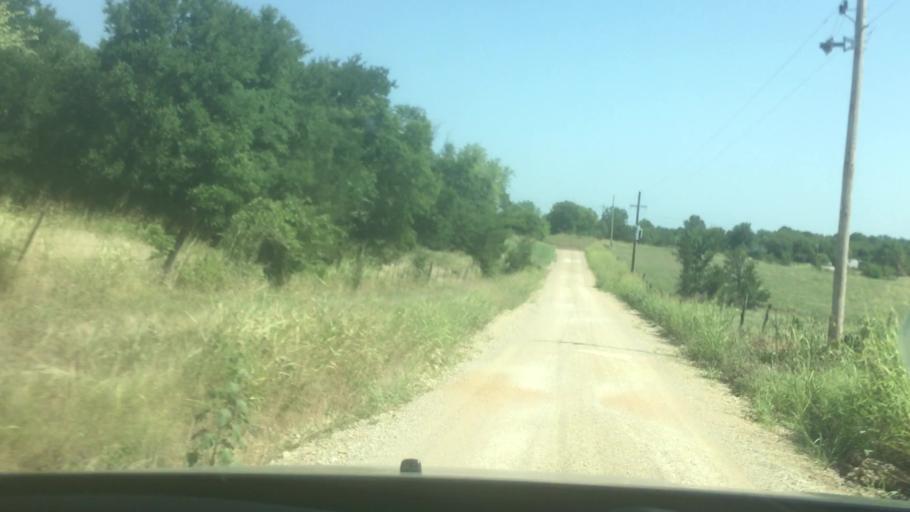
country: US
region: Oklahoma
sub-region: Bryan County
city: Durant
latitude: 34.1407
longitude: -96.4077
